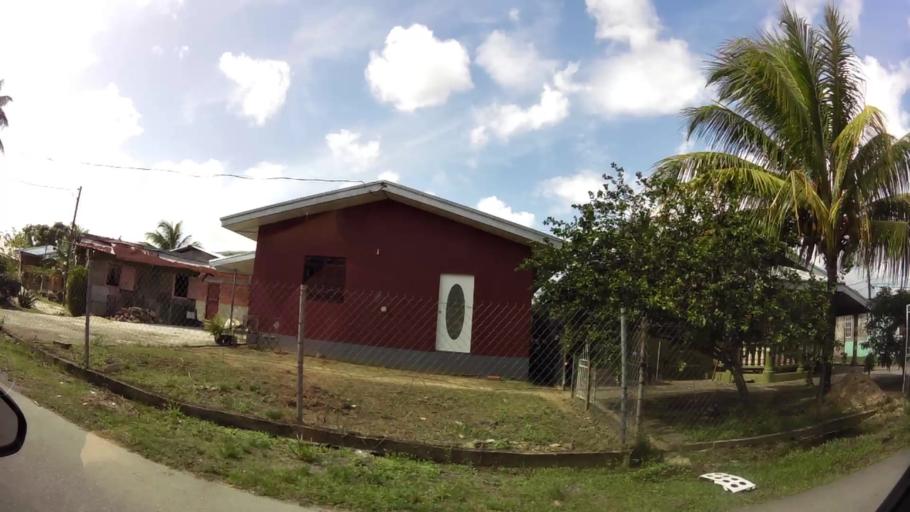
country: TT
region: Borough of Arima
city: Arima
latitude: 10.6214
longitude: -61.2560
